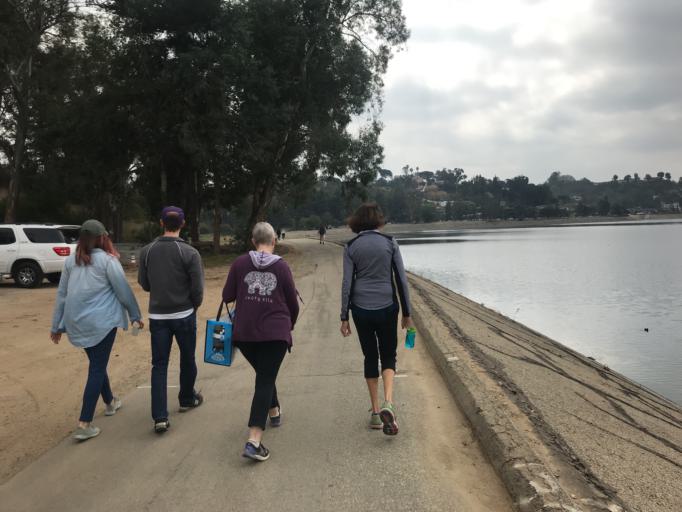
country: US
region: California
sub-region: Los Angeles County
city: Silver Lake
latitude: 34.0998
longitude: -118.2629
